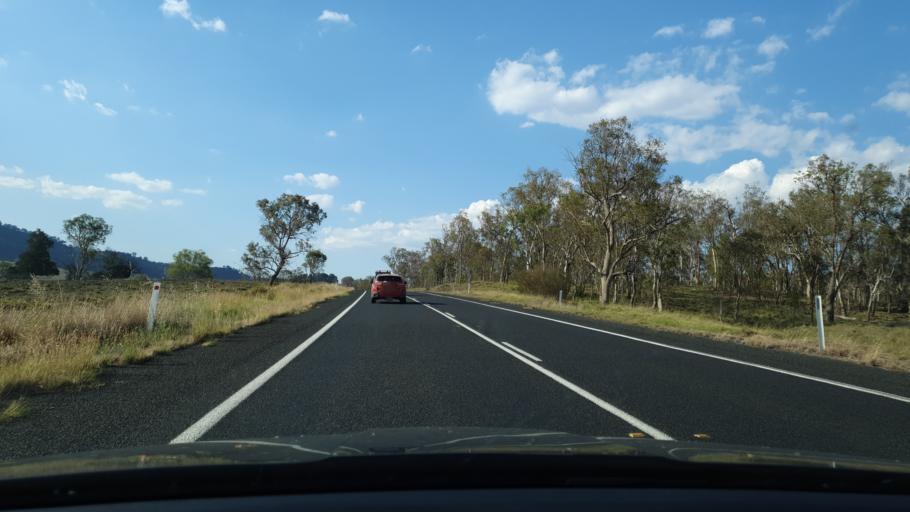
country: AU
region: New South Wales
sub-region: Tenterfield Municipality
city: Carrolls Creek
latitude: -29.1510
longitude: 152.0013
